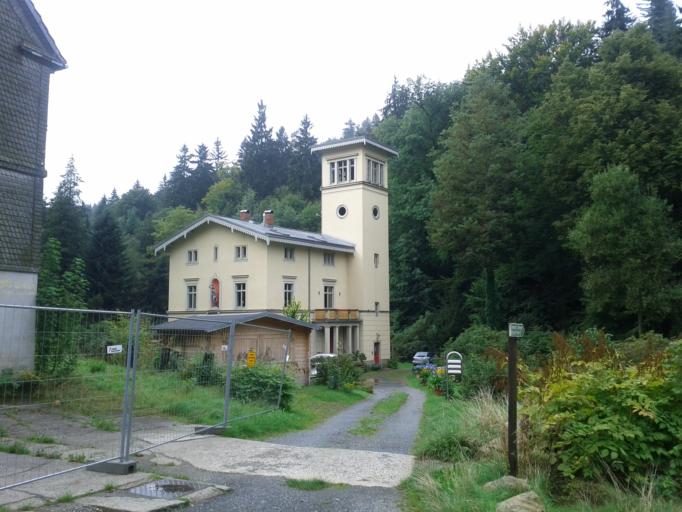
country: DE
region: Saxony
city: Konigstein
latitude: 50.8482
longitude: 14.0438
